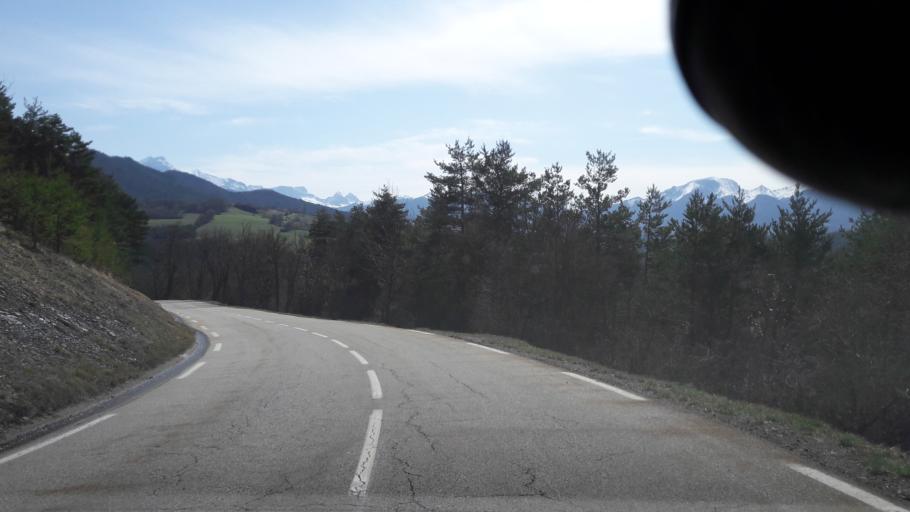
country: FR
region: Rhone-Alpes
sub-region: Departement de l'Isere
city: La Motte-Saint-Martin
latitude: 44.8702
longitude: 5.6579
